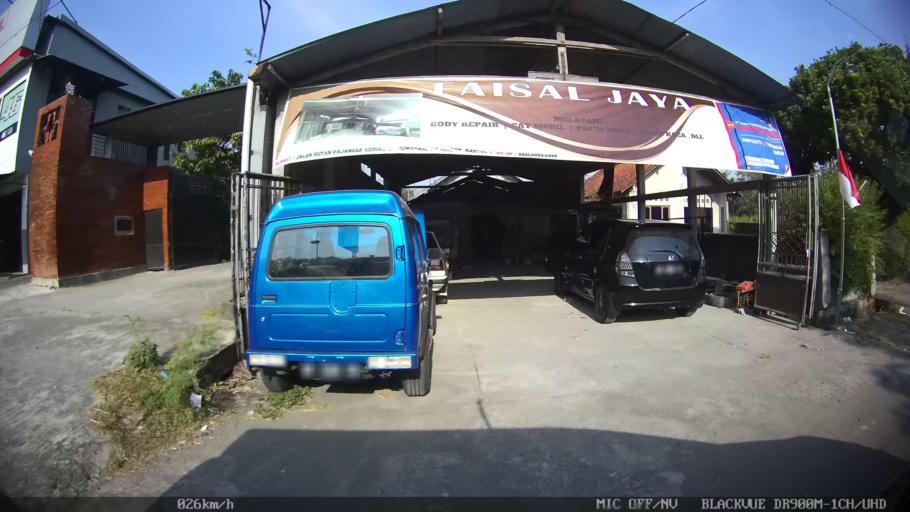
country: ID
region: Daerah Istimewa Yogyakarta
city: Bantul
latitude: -7.8847
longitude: 110.3048
